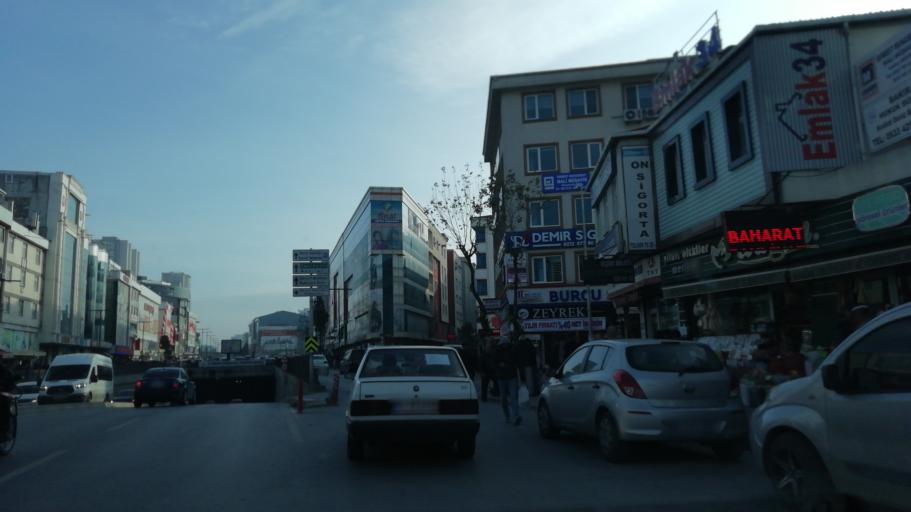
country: TR
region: Istanbul
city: Esenyurt
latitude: 41.0368
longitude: 28.6789
